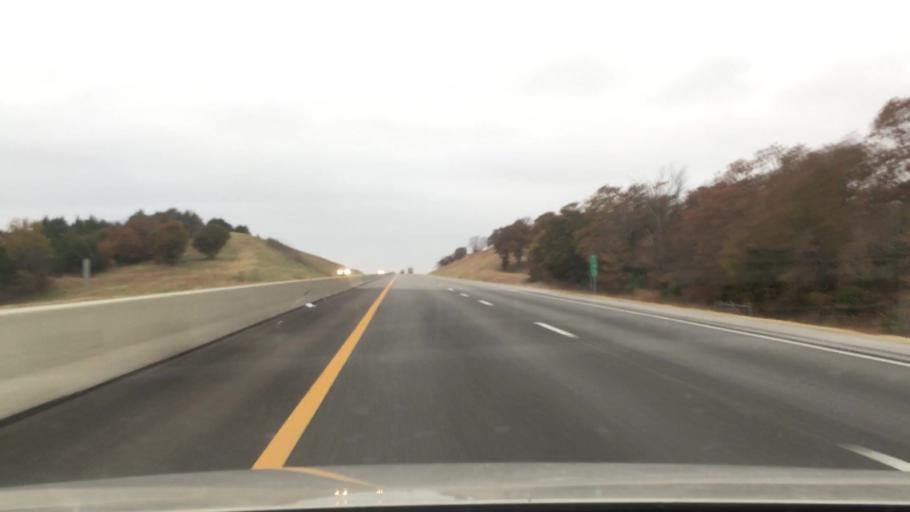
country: US
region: Oklahoma
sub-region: Lincoln County
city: Chandler
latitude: 35.7379
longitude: -96.7803
